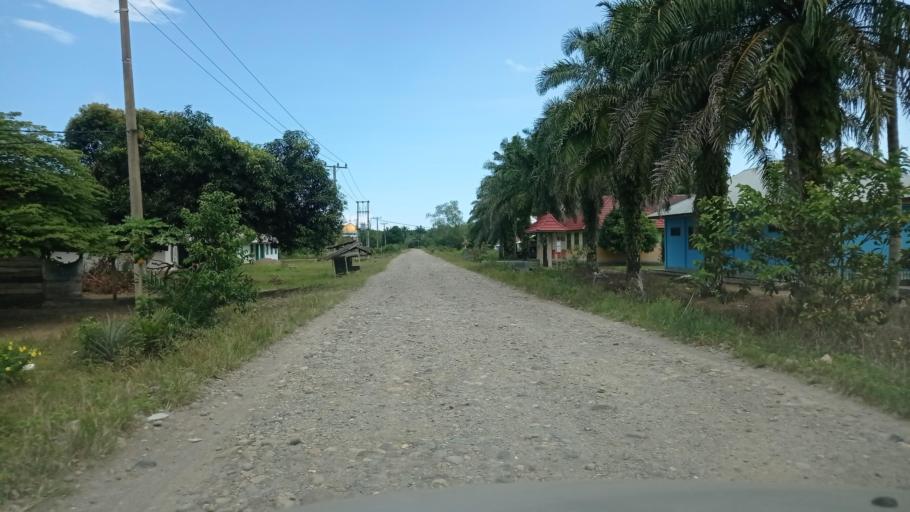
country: ID
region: Jambi
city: Sungai Penuh
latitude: -2.4847
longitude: 101.0705
